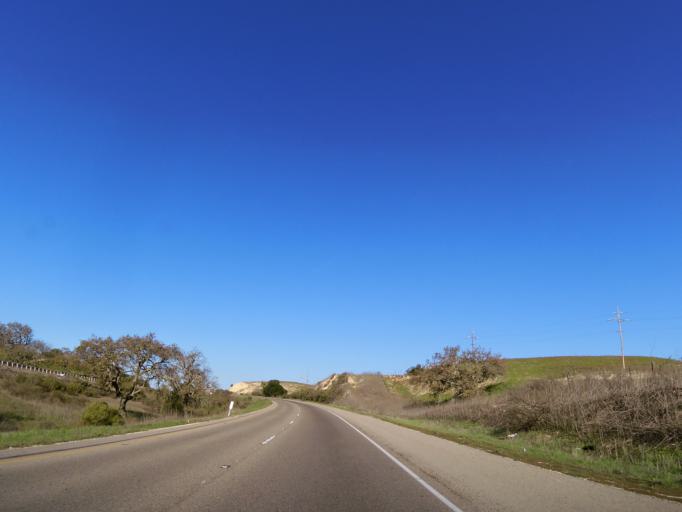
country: US
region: California
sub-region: Santa Barbara County
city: Los Olivos
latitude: 34.7070
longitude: -120.1710
